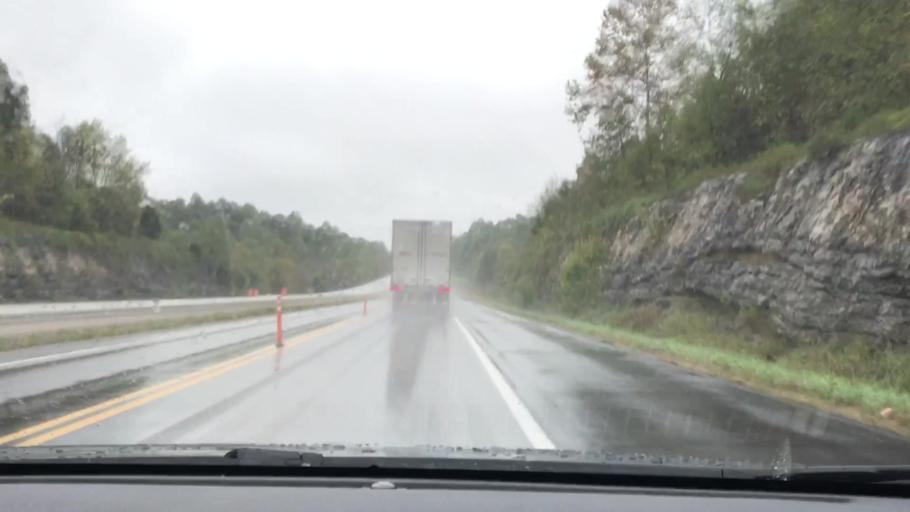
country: US
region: Kentucky
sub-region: Christian County
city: Hopkinsville
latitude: 37.0027
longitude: -87.4626
